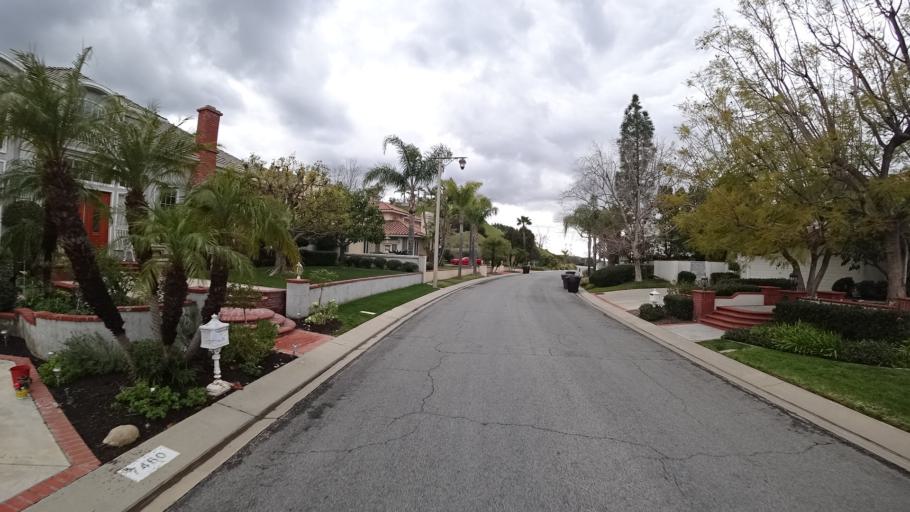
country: US
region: California
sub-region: Orange County
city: Villa Park
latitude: 33.8494
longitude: -117.7548
